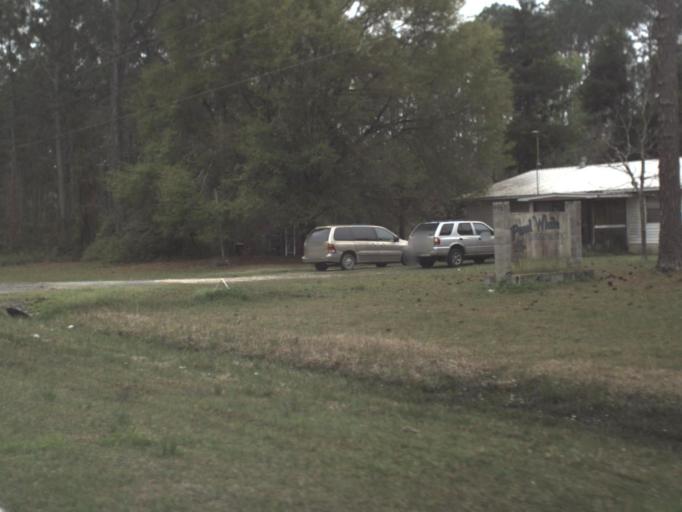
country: US
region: Florida
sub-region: Liberty County
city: Bristol
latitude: 30.3207
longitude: -84.8256
